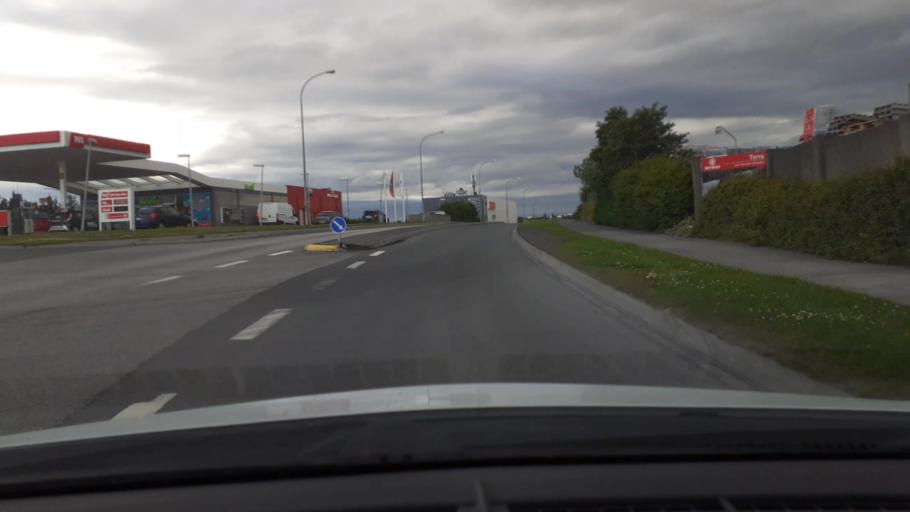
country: IS
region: Capital Region
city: Reykjavik
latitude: 64.1247
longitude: -21.8277
